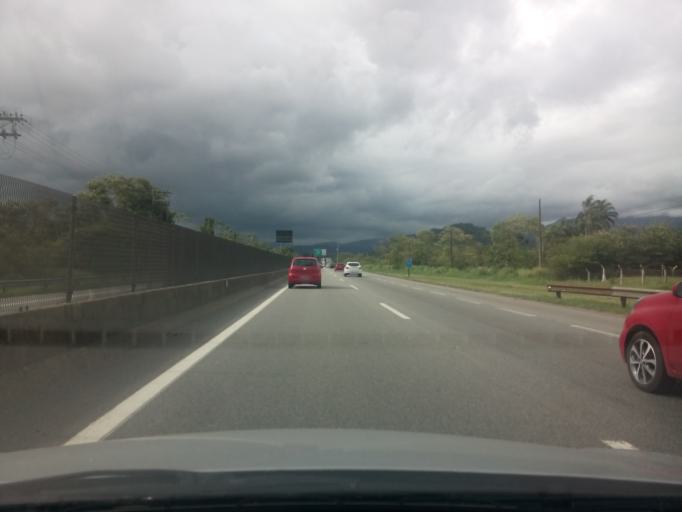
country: BR
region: Sao Paulo
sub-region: Santos
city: Santos
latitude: -23.9342
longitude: -46.2829
